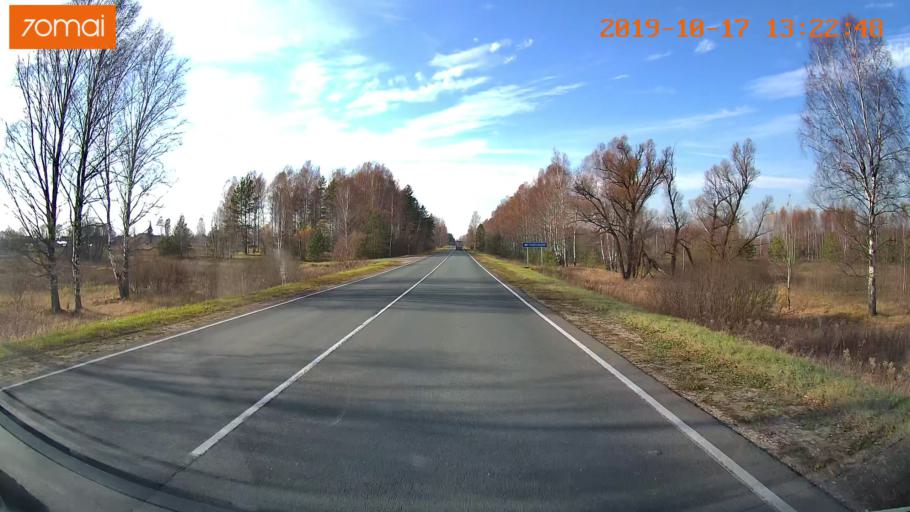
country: RU
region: Rjazan
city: Gus'-Zheleznyy
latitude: 55.0870
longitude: 40.9937
